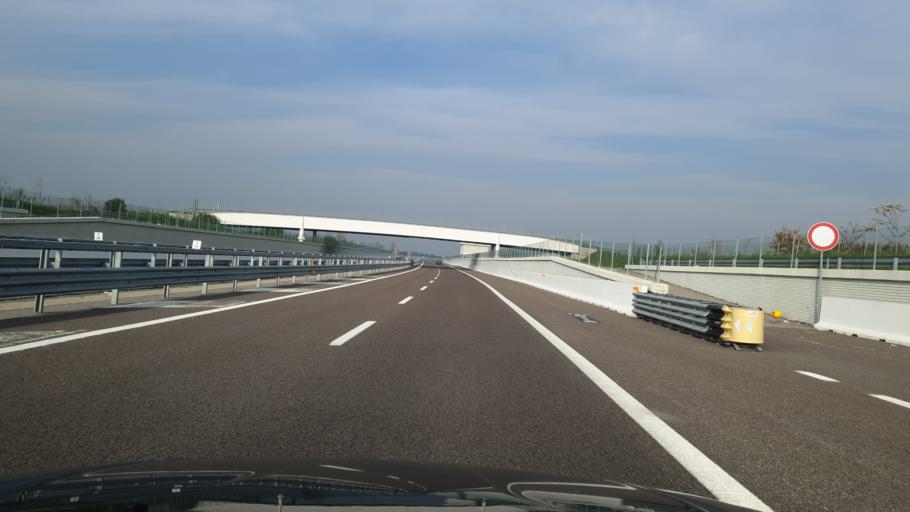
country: IT
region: Veneto
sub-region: Provincia di Vicenza
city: Agugliaro
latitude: 45.3141
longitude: 11.5786
